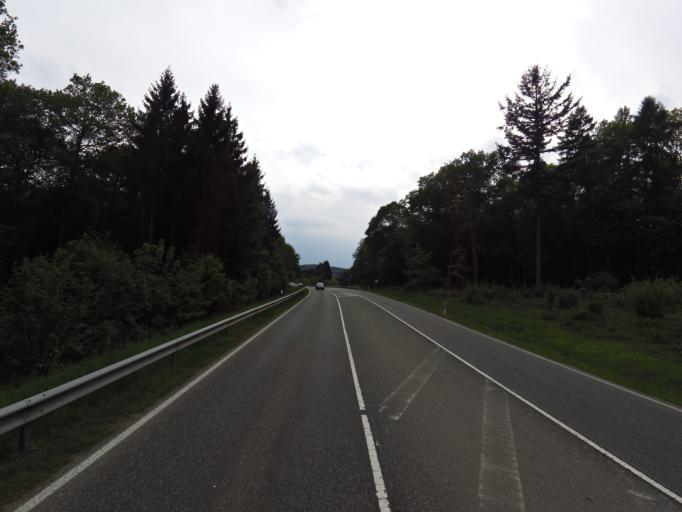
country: DE
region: Rheinland-Pfalz
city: Waldesch
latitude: 50.2559
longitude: 7.5254
